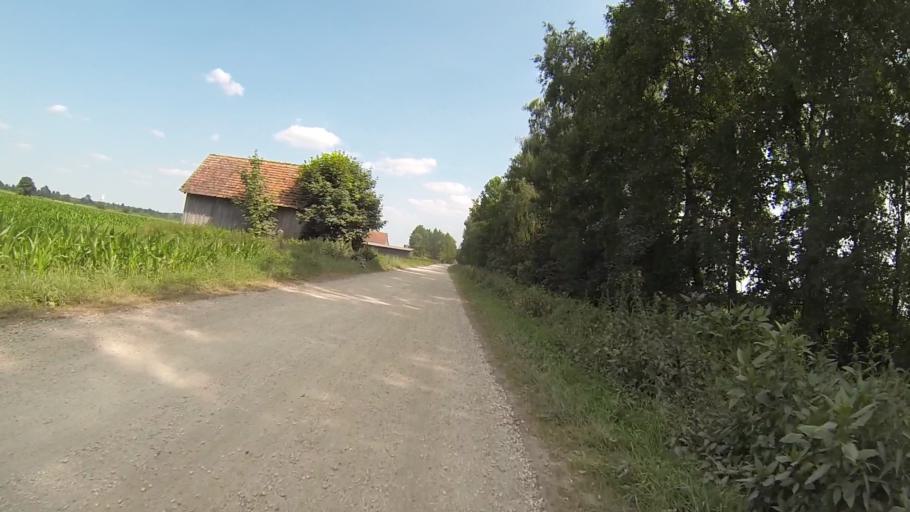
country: DE
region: Bavaria
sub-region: Swabia
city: Guenzburg
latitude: 48.4938
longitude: 10.2735
